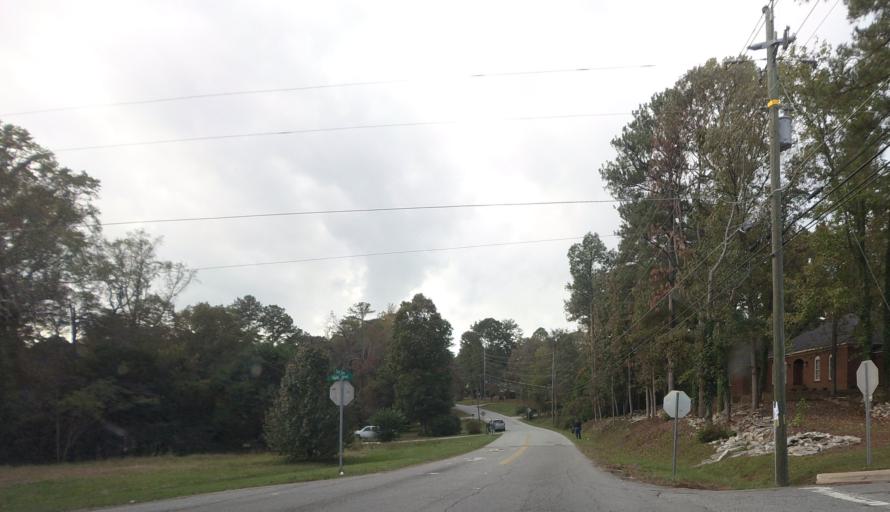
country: US
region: Georgia
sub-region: Houston County
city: Centerville
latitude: 32.6270
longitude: -83.6556
